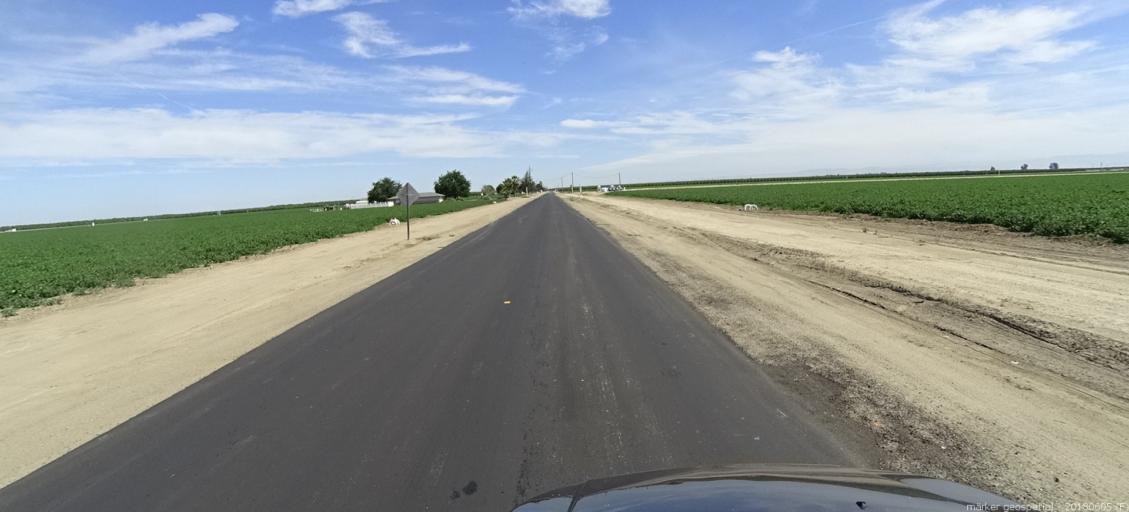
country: US
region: California
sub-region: Madera County
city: Chowchilla
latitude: 37.0847
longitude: -120.3827
